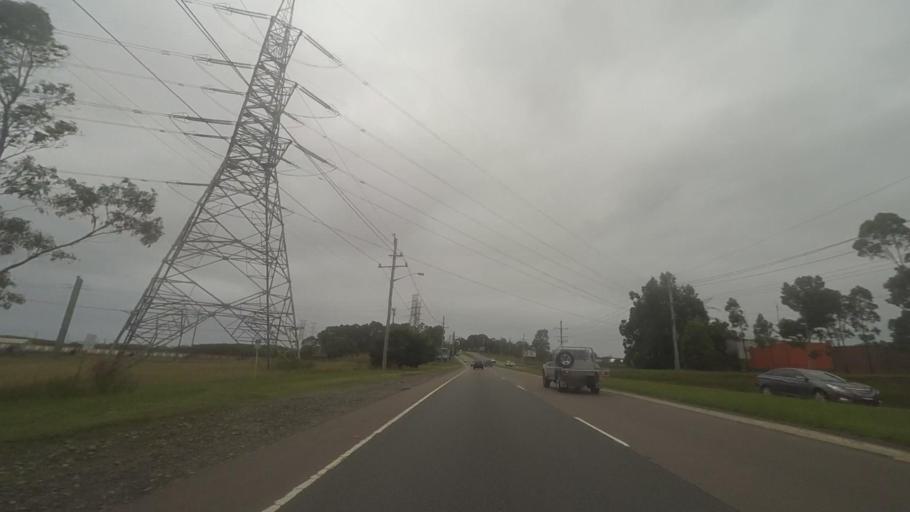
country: AU
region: New South Wales
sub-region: Newcastle
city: Mayfield West
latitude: -32.8749
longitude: 151.7128
